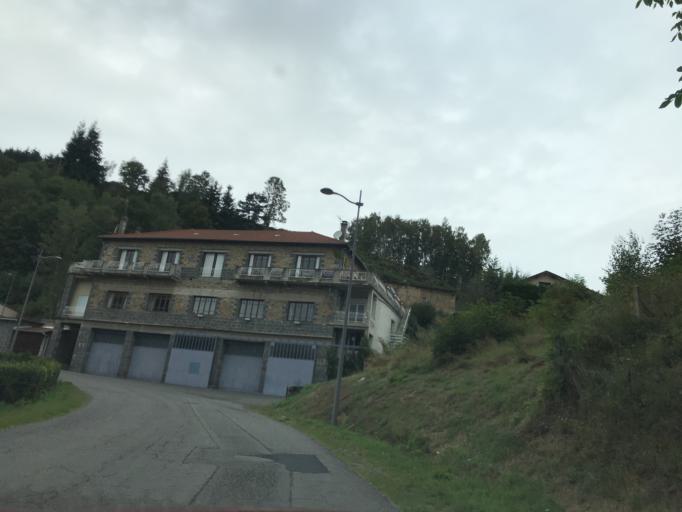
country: FR
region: Rhone-Alpes
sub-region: Departement de la Loire
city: Sail-sous-Couzan
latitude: 45.7060
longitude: 3.8502
